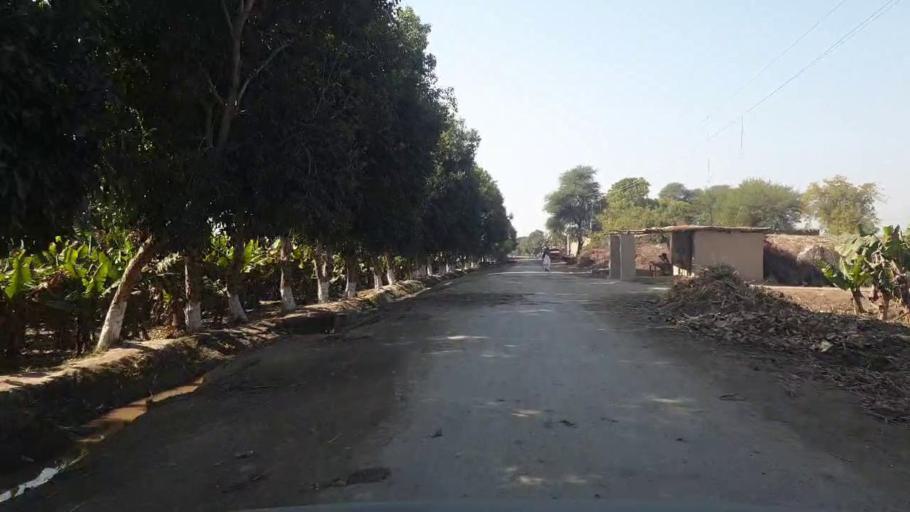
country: PK
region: Sindh
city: Chambar
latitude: 25.3693
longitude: 68.7776
